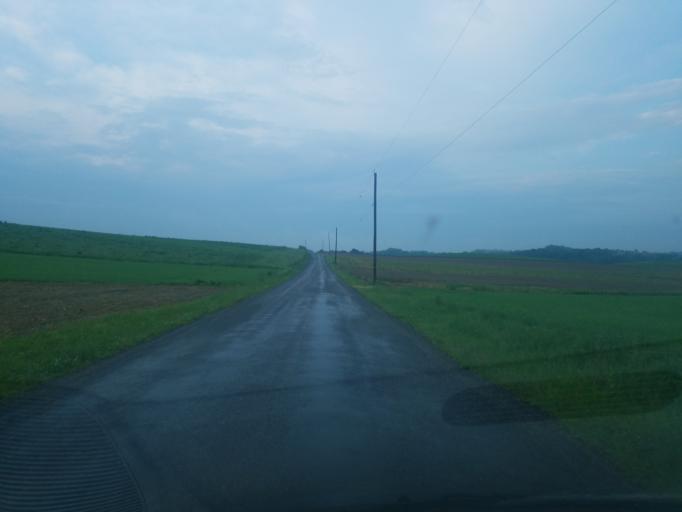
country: US
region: Ohio
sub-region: Mahoning County
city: Sebring
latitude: 40.7886
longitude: -80.9555
